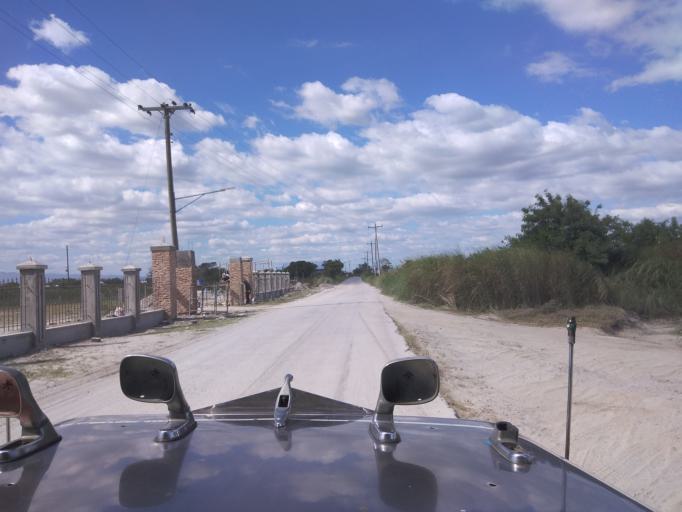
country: PH
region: Central Luzon
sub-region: Province of Pampanga
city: Magliman
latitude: 15.0409
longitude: 120.6304
